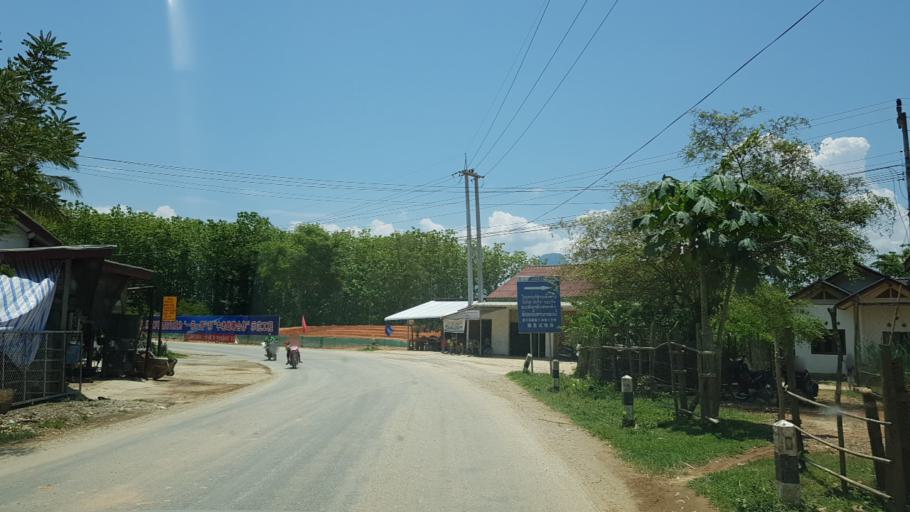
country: LA
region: Vientiane
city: Muang Kasi
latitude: 19.2520
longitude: 102.2390
